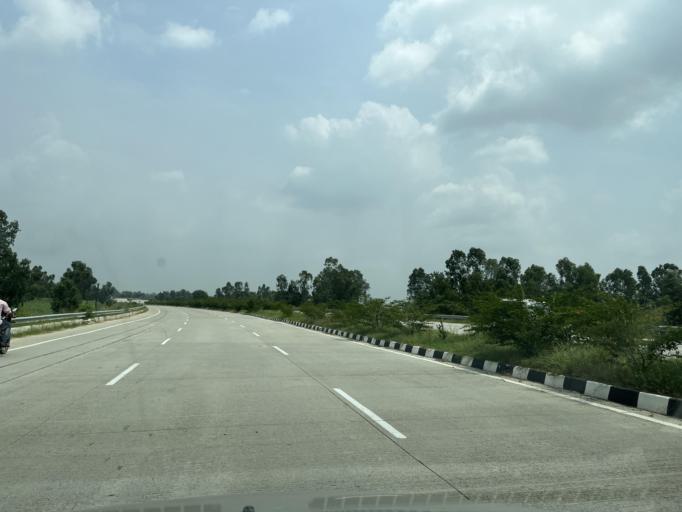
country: IN
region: Uttar Pradesh
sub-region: Bijnor
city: Nagina
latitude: 29.4313
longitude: 78.4061
